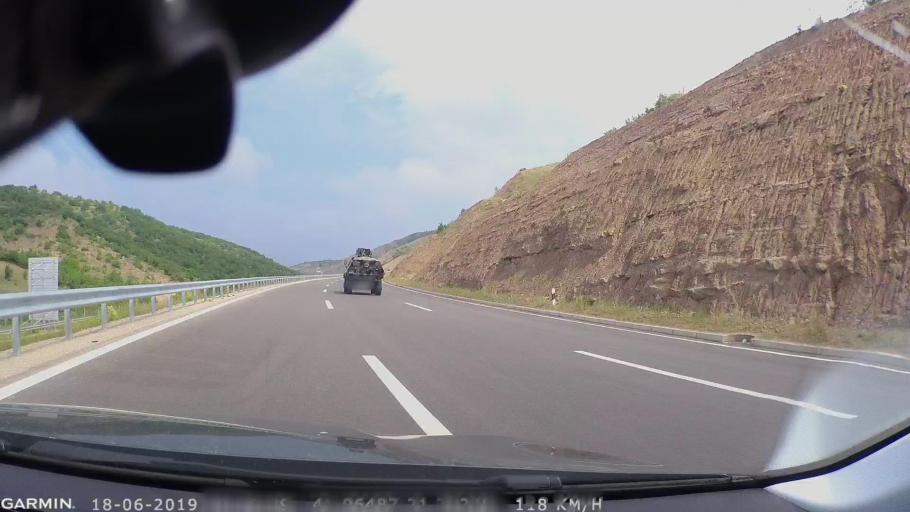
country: MK
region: Petrovec
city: Sredno Konjare
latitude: 41.9468
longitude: 21.7968
